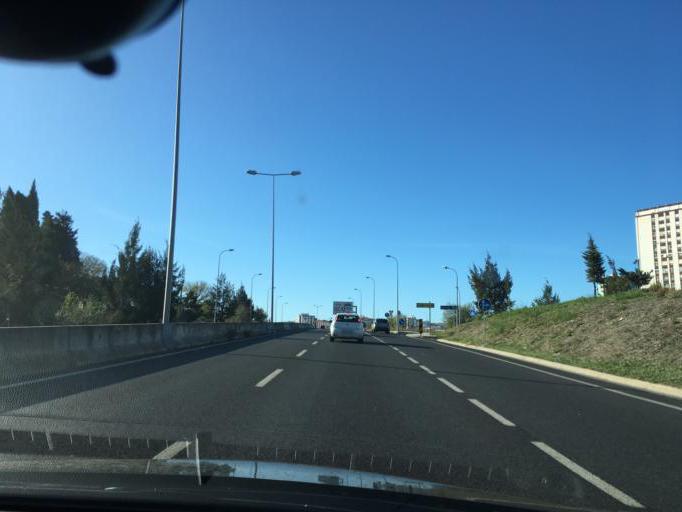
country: PT
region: Lisbon
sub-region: Odivelas
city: Pontinha
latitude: 38.7589
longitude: -9.1970
